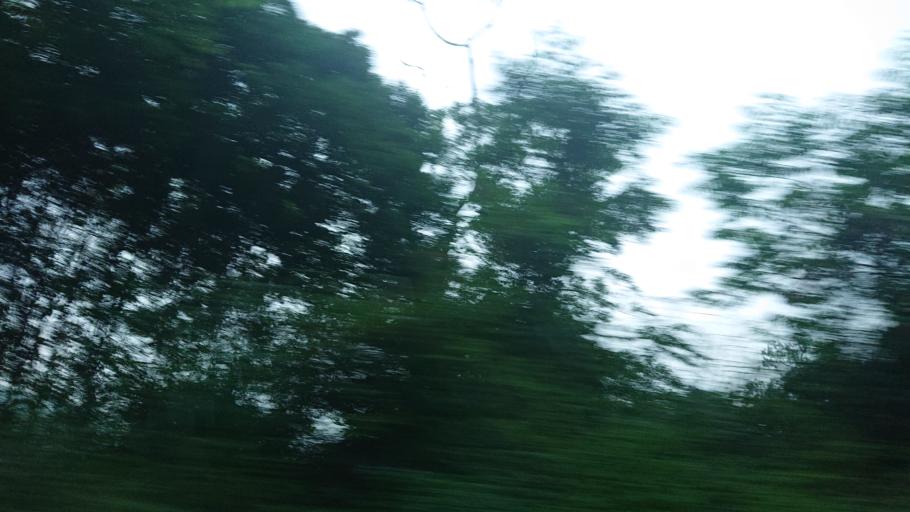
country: TW
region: Taiwan
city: Lugu
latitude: 23.5972
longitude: 120.7208
